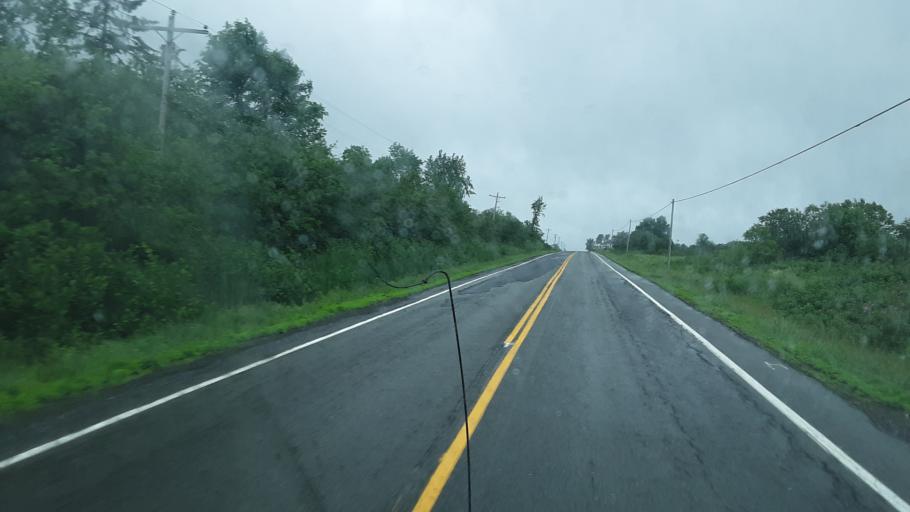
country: US
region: Maine
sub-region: Penobscot County
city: Patten
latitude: 46.0377
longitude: -68.4442
